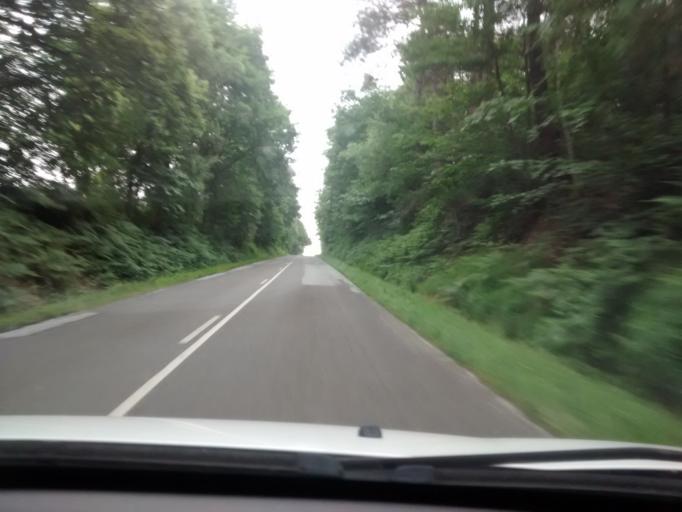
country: FR
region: Brittany
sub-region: Departement d'Ille-et-Vilaine
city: La Bouexiere
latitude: 48.1596
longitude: -1.4412
